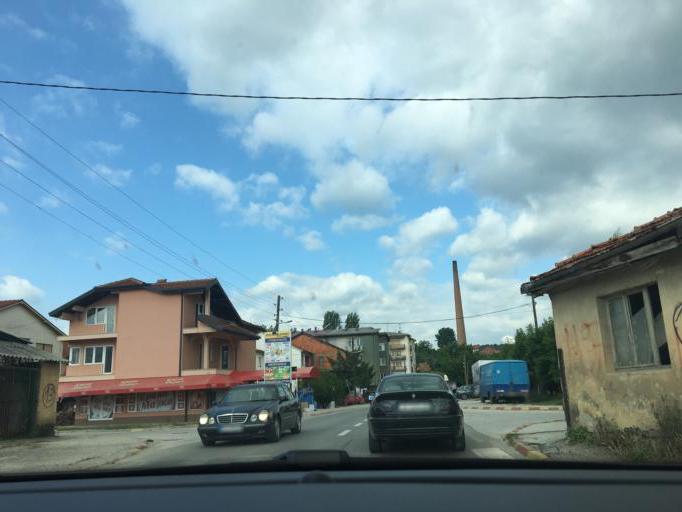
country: MK
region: Resen
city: Resen
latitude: 41.0853
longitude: 21.0110
